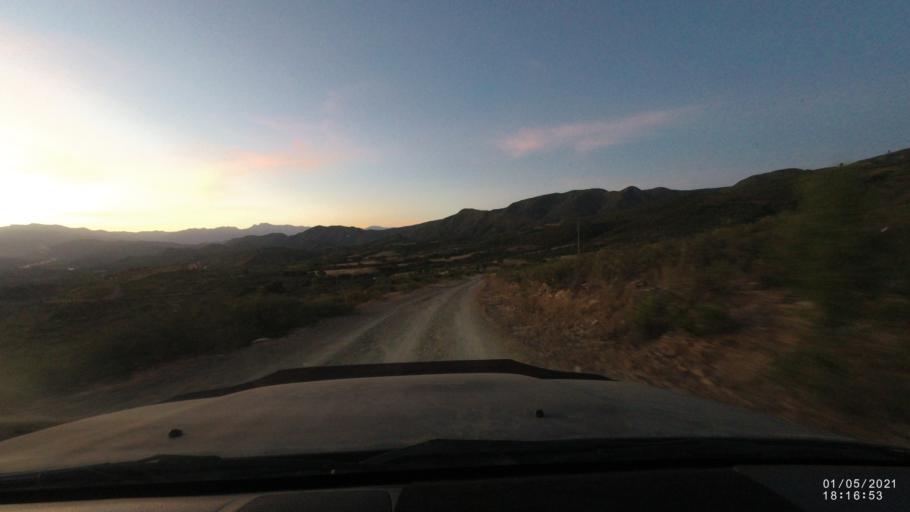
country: BO
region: Cochabamba
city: Capinota
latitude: -17.6692
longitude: -66.2182
